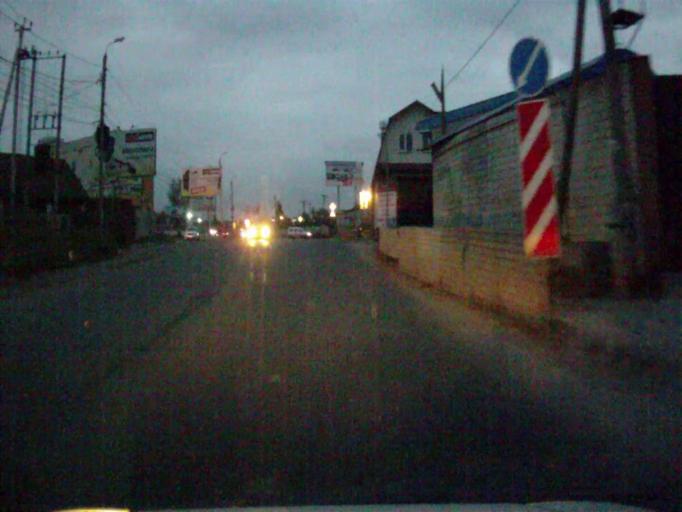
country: RU
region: Chelyabinsk
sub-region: Gorod Chelyabinsk
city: Chelyabinsk
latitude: 55.1547
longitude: 61.3022
